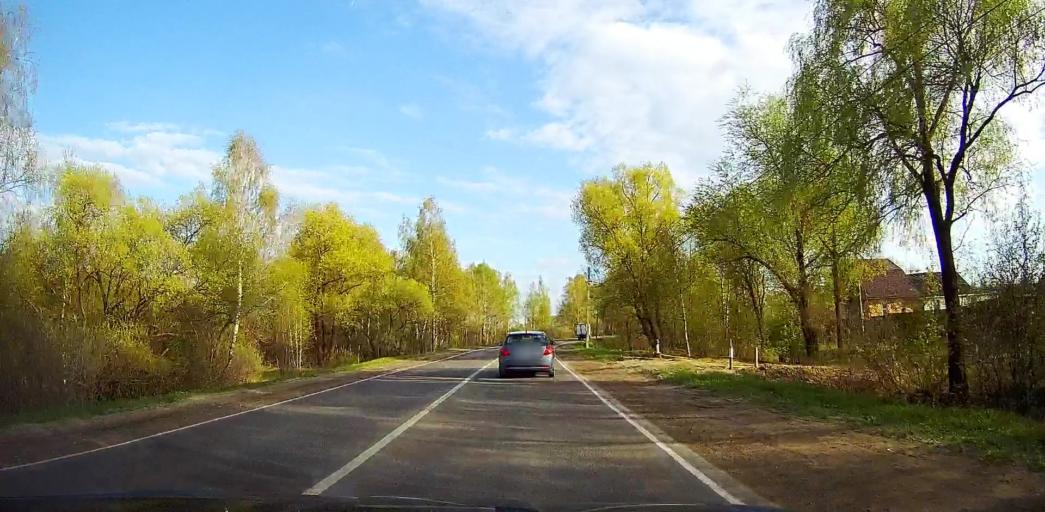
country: RU
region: Moskovskaya
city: Fryazevo
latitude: 55.7207
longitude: 38.4675
